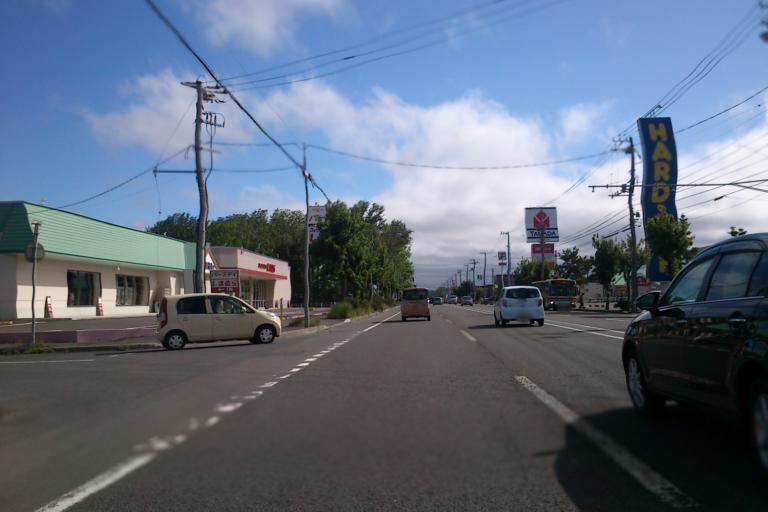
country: JP
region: Hokkaido
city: Sapporo
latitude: 43.1484
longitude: 141.2837
